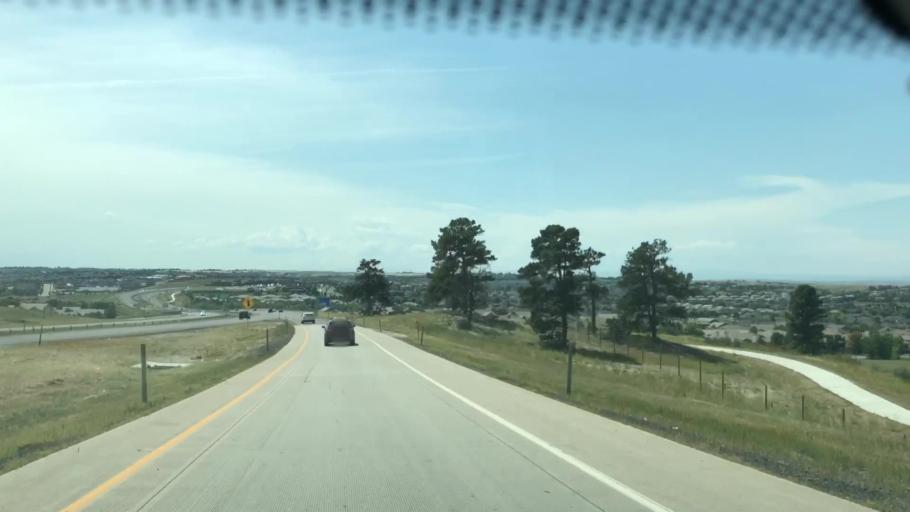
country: US
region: Colorado
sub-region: Douglas County
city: Parker
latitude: 39.5983
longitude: -104.7175
